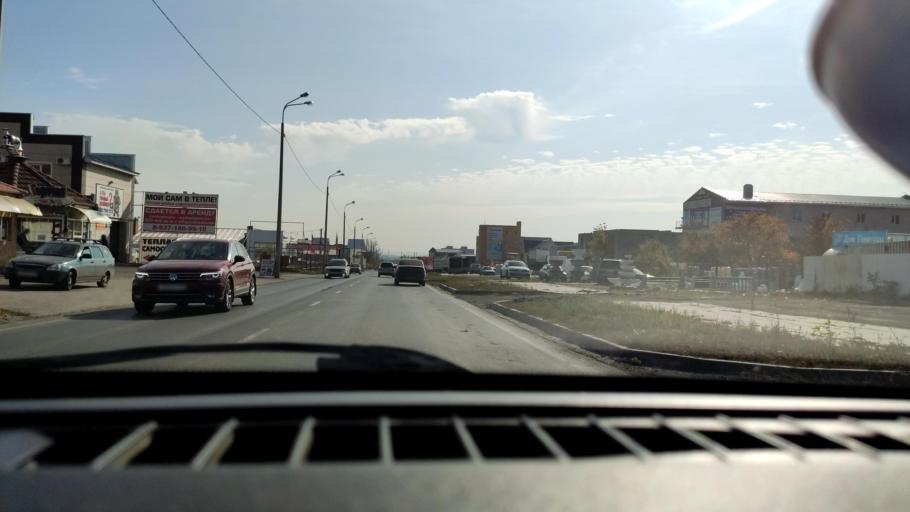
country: RU
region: Samara
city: Petra-Dubrava
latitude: 53.2647
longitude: 50.2611
